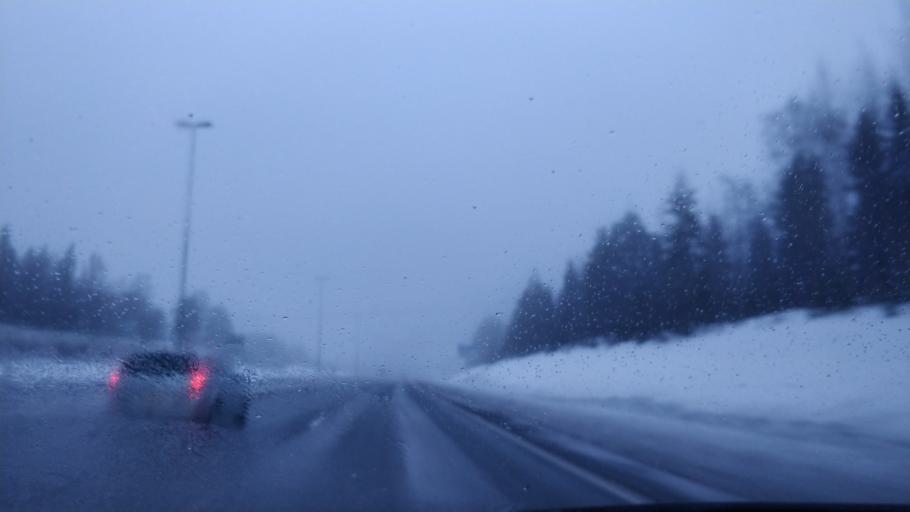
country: FI
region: Lapland
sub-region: Kemi-Tornio
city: Kemi
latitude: 65.7518
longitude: 24.5747
